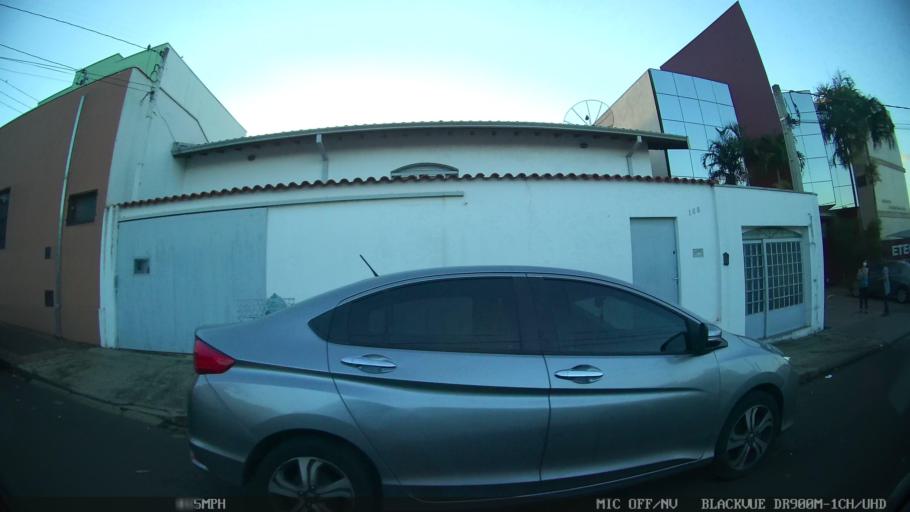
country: BR
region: Sao Paulo
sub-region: Santa Barbara D'Oeste
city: Santa Barbara d'Oeste
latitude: -22.7515
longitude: -47.4104
